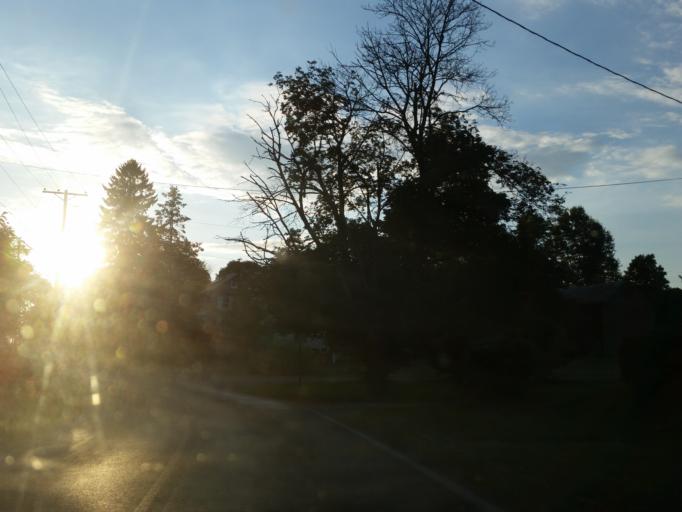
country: US
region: Pennsylvania
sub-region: Berks County
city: Alleghenyville
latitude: 40.2454
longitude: -75.9996
